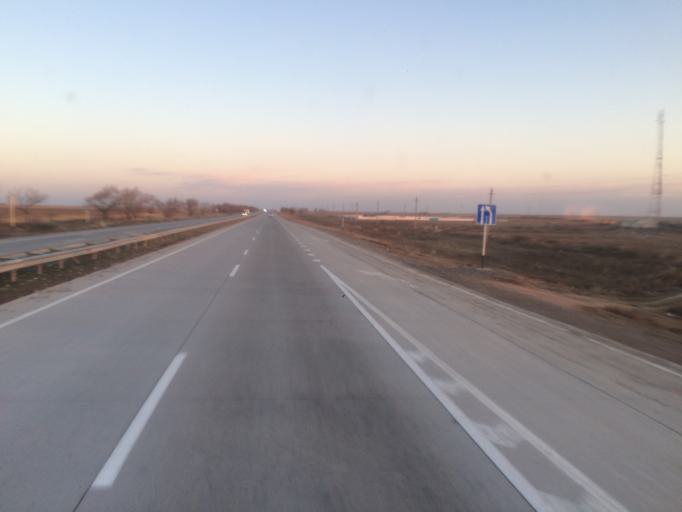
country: KZ
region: Ongtustik Qazaqstan
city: Bayaldyr
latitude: 43.0607
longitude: 68.6833
